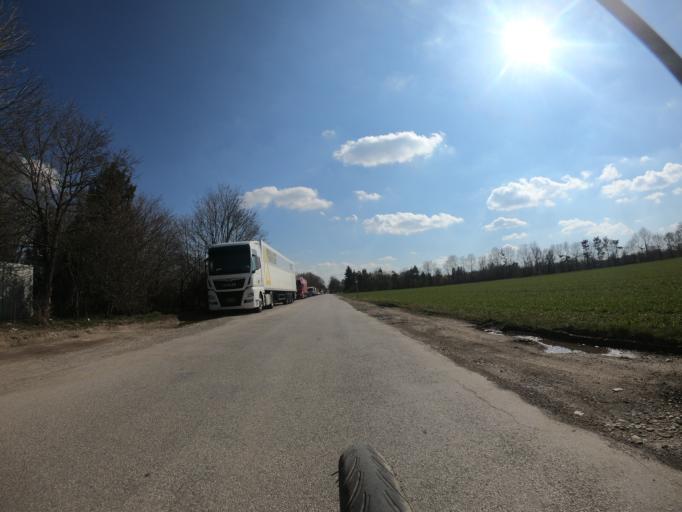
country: DE
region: Bavaria
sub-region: Upper Bavaria
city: Fuerstenfeldbruck
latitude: 48.2001
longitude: 11.2445
